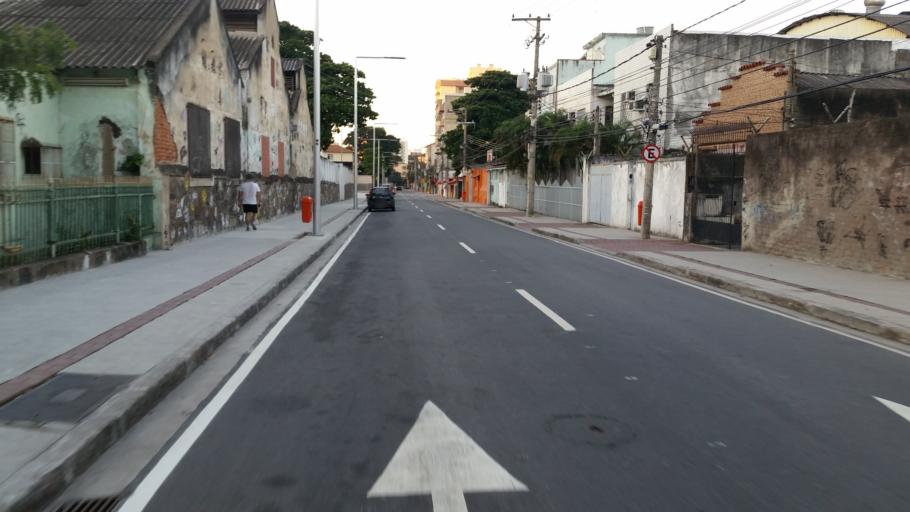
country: BR
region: Rio de Janeiro
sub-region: Rio De Janeiro
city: Rio de Janeiro
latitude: -22.8951
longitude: -43.2908
